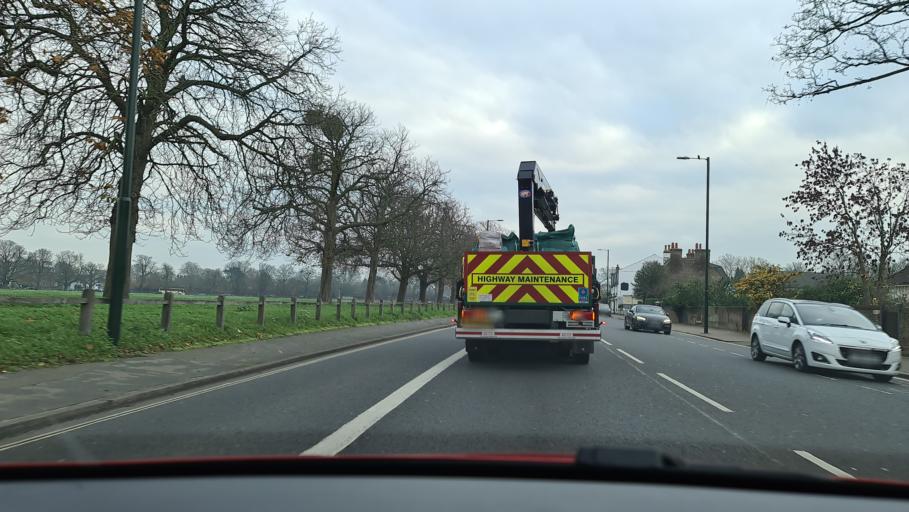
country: GB
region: England
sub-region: Surrey
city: East Molesey
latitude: 51.4073
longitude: -0.3455
